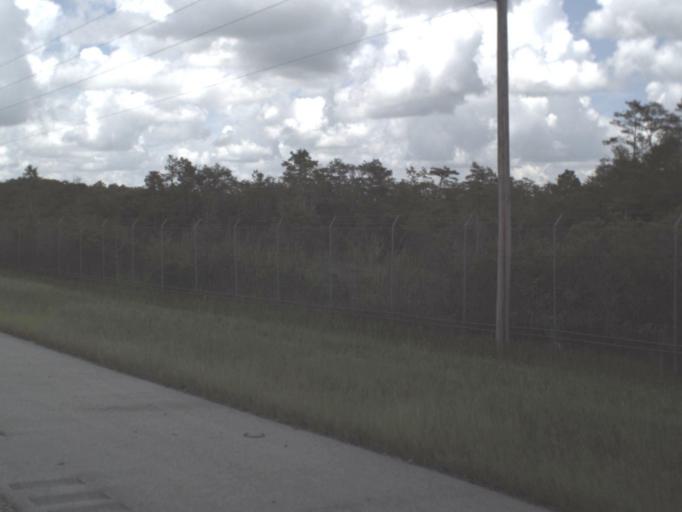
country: US
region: Florida
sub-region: Broward County
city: Weston
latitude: 26.1718
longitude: -80.9320
